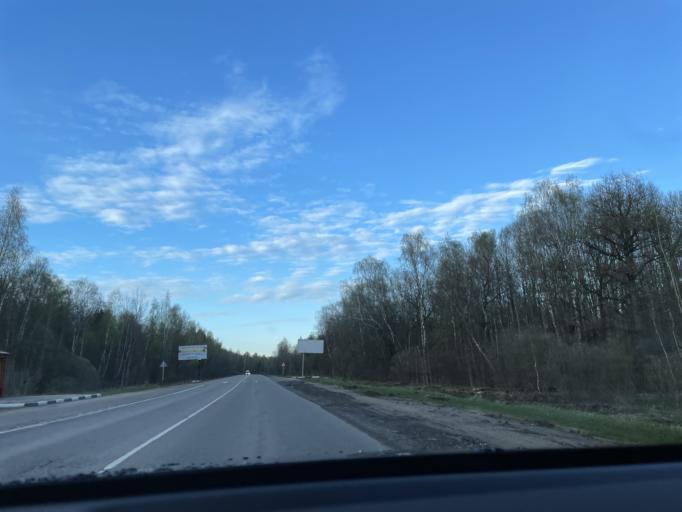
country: RU
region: Tula
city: Aleksin
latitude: 54.5150
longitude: 37.1397
